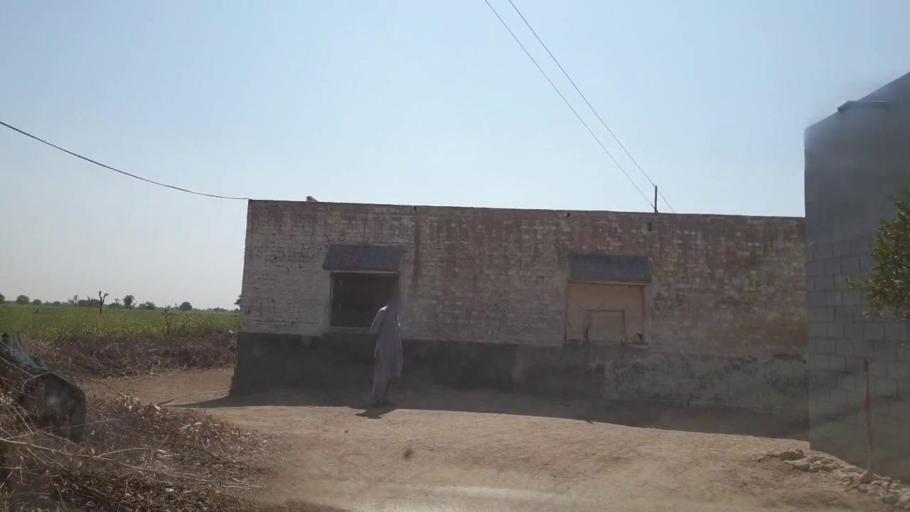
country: PK
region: Sindh
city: Mirpur Khas
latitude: 25.7215
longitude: 69.1082
